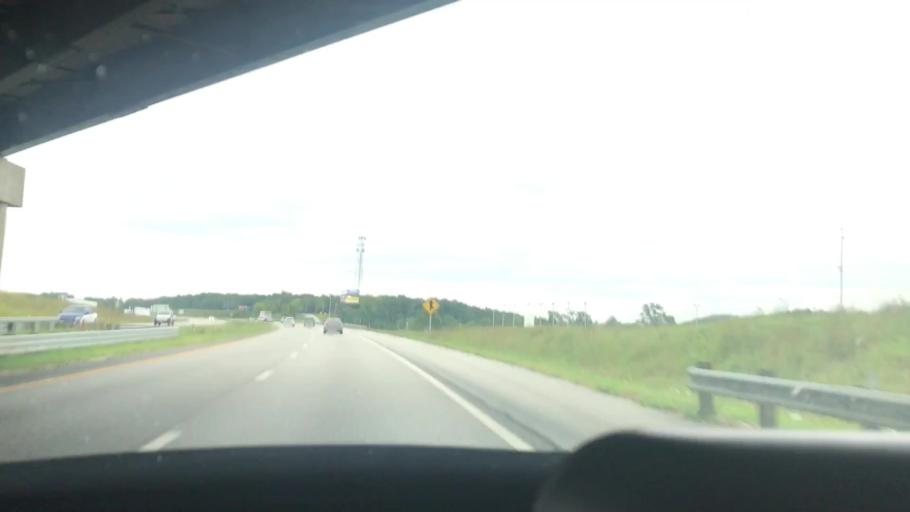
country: US
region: Missouri
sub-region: Jasper County
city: Joplin
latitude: 37.0098
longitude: -94.5478
